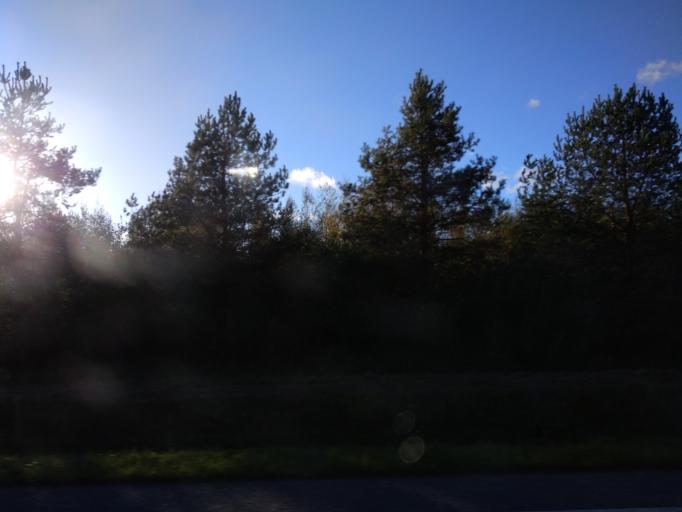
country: EE
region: Polvamaa
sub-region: Polva linn
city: Polva
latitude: 58.0308
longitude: 27.0660
